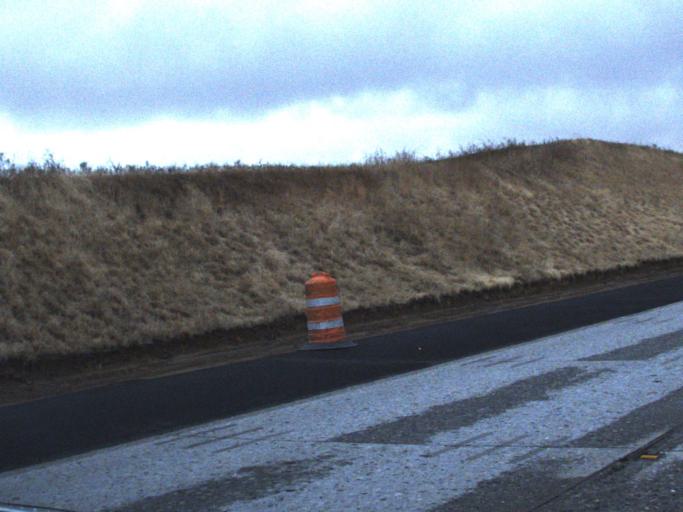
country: US
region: Washington
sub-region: Whitman County
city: Colfax
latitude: 47.0258
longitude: -117.3601
